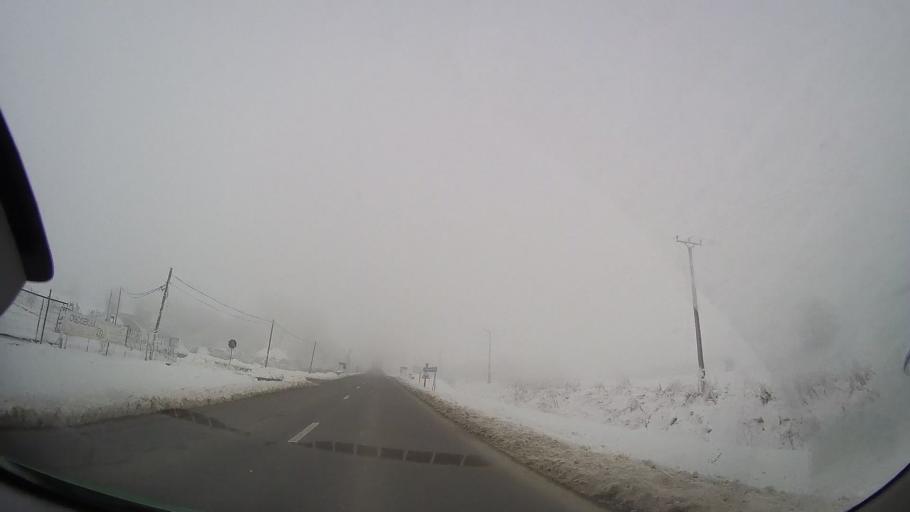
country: RO
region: Iasi
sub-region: Comuna Stolniceni-Prajescu
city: Stolniceni-Prajescu
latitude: 47.1916
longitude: 26.7373
